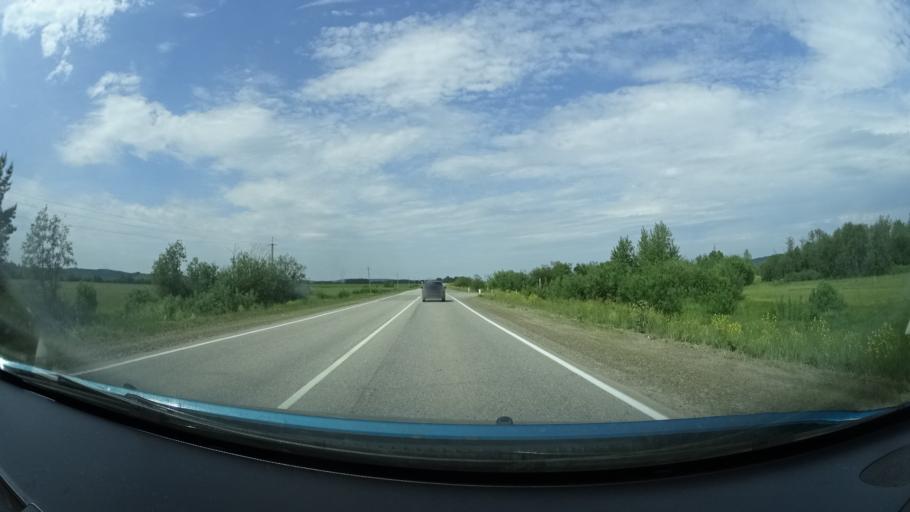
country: RU
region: Perm
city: Barda
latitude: 57.0559
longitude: 55.5433
